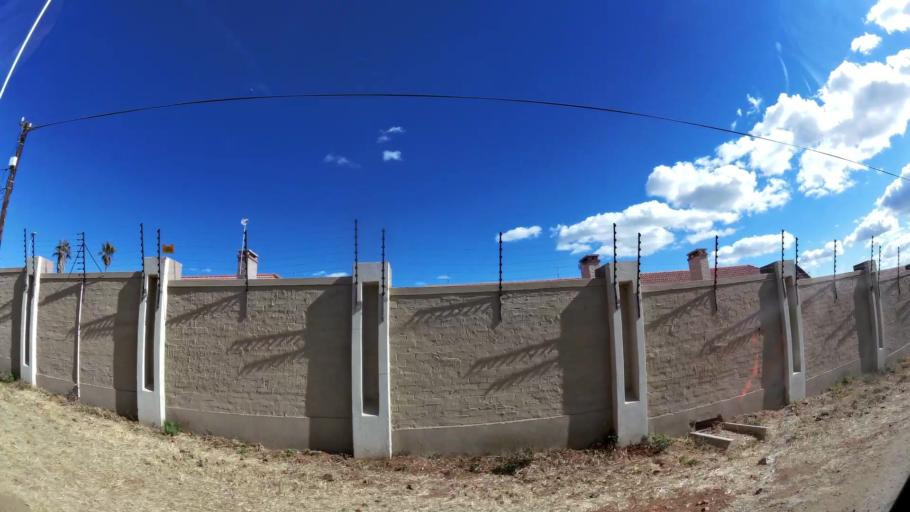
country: ZA
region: Limpopo
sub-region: Capricorn District Municipality
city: Polokwane
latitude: -23.8784
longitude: 29.5153
